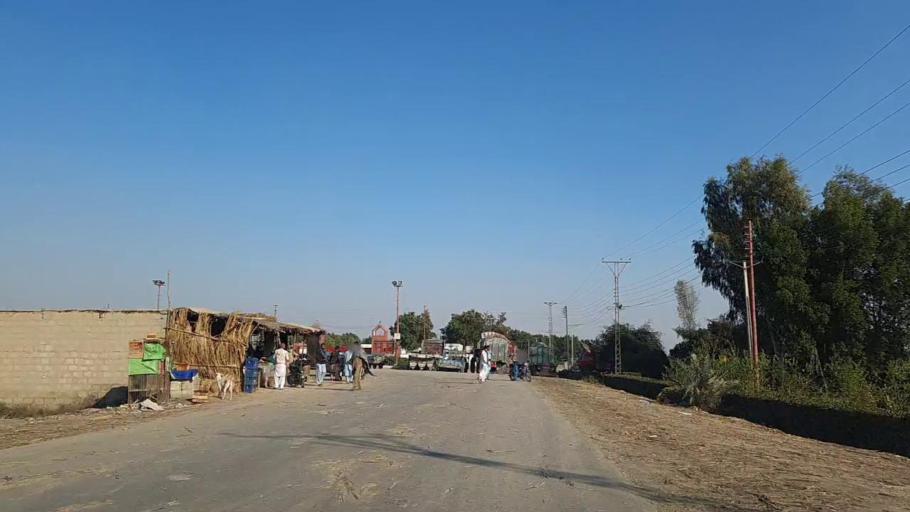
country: PK
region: Sindh
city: Bandhi
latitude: 26.6051
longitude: 68.3151
